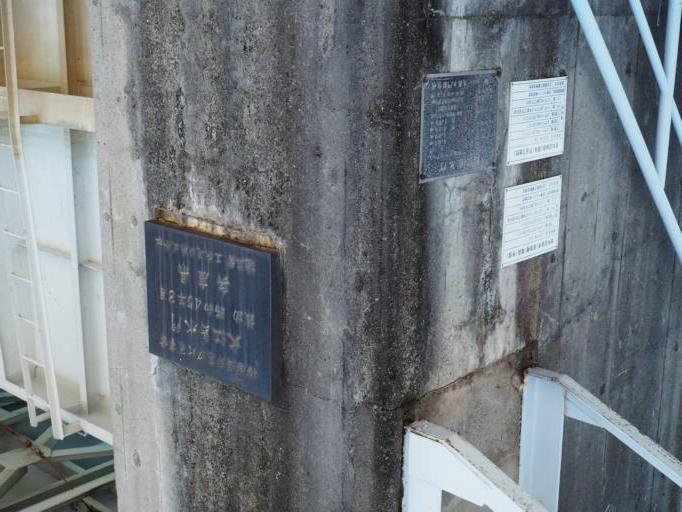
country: JP
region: Hyogo
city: Tatsunocho-tominaga
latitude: 34.7858
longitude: 134.5996
